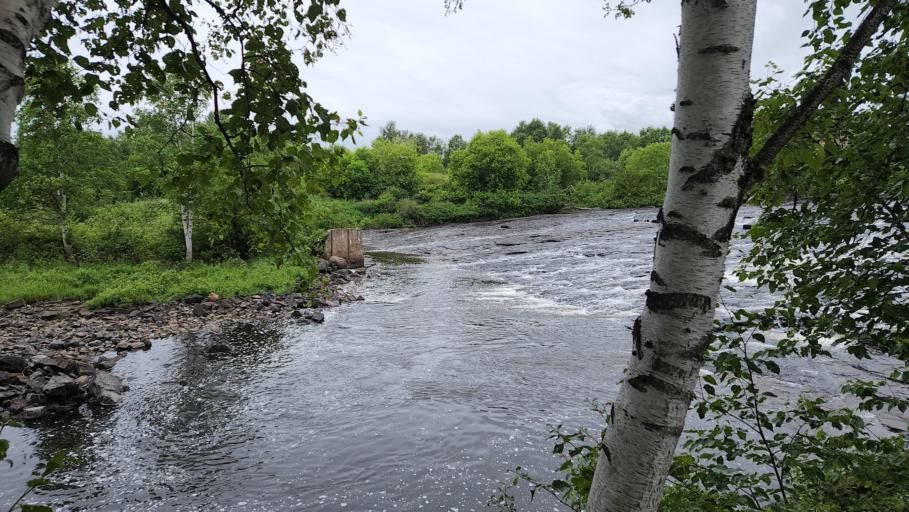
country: CA
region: Ontario
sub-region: Thunder Bay District
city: Thunder Bay
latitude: 48.4526
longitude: -89.1837
